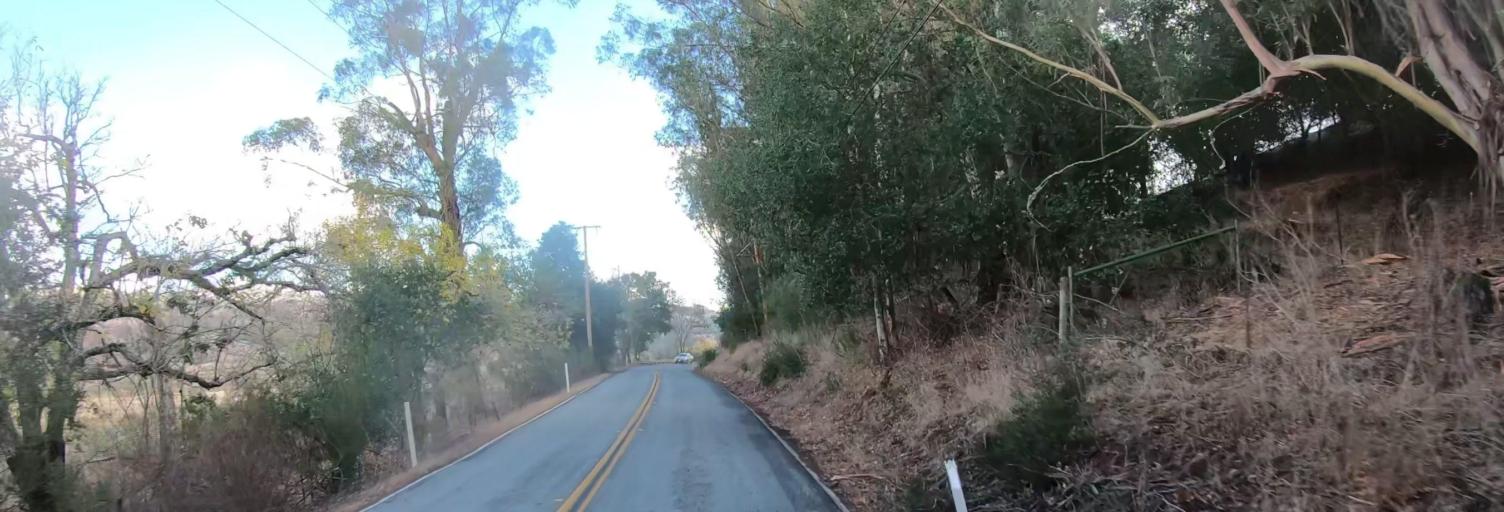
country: US
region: California
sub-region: Santa Clara County
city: East Foothills
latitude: 37.3431
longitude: -121.7232
